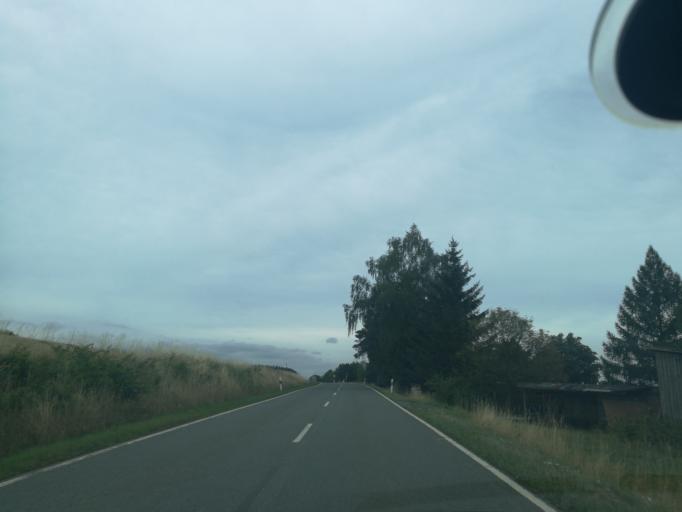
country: DE
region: Bavaria
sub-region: Upper Franconia
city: Regnitzlosau
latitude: 50.3245
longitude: 12.0659
